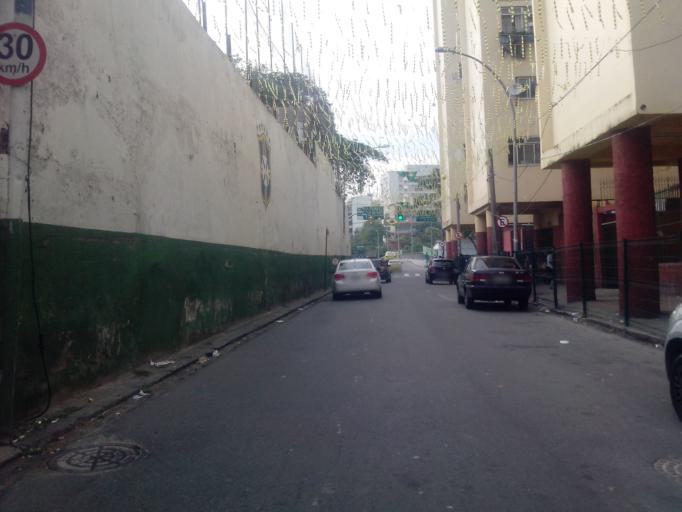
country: BR
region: Rio de Janeiro
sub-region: Rio De Janeiro
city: Rio de Janeiro
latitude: -22.9816
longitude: -43.2158
